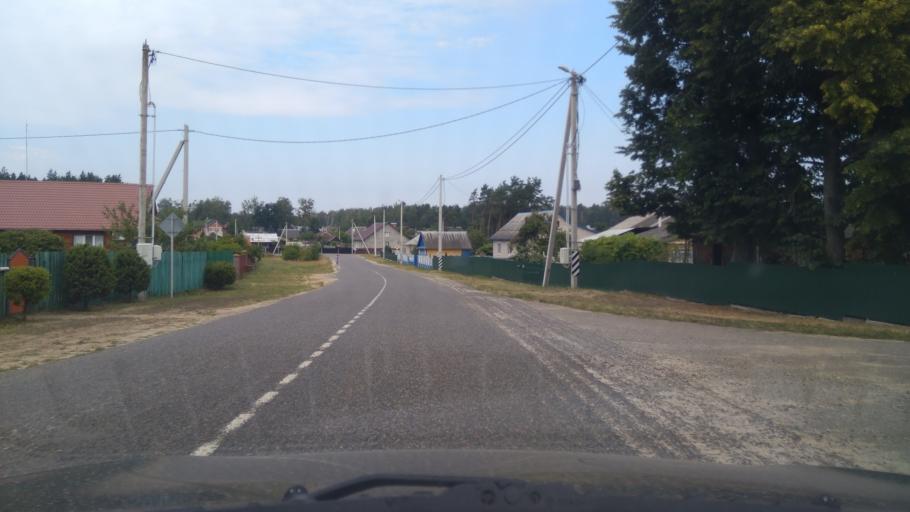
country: BY
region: Brest
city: Nyakhachava
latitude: 52.6096
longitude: 25.0888
